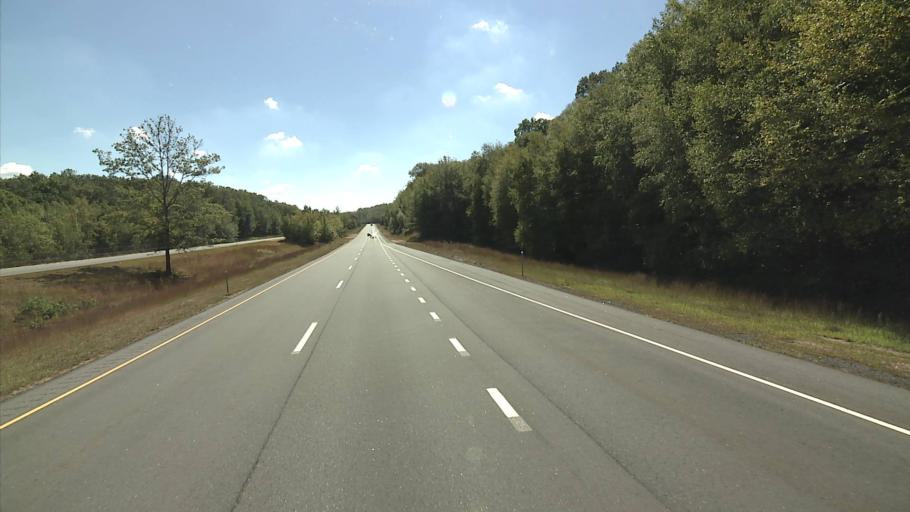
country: US
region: Connecticut
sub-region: New London County
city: Colchester
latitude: 41.4968
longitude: -72.3022
